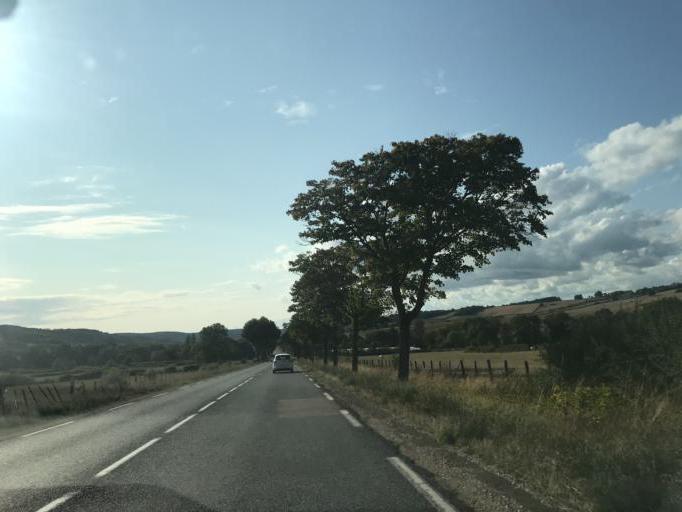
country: FR
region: Bourgogne
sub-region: Departement de l'Yonne
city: Avallon
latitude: 47.5074
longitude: 3.8573
